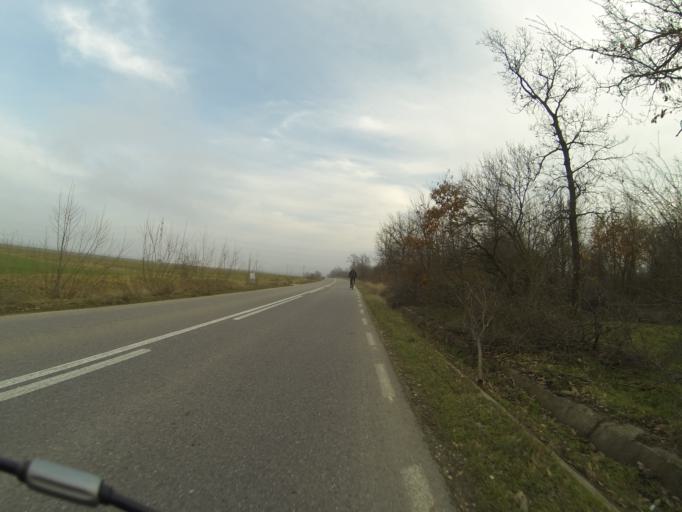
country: RO
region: Mehedinti
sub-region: Comuna Corlatel
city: Corlatel
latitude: 44.4011
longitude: 22.9082
